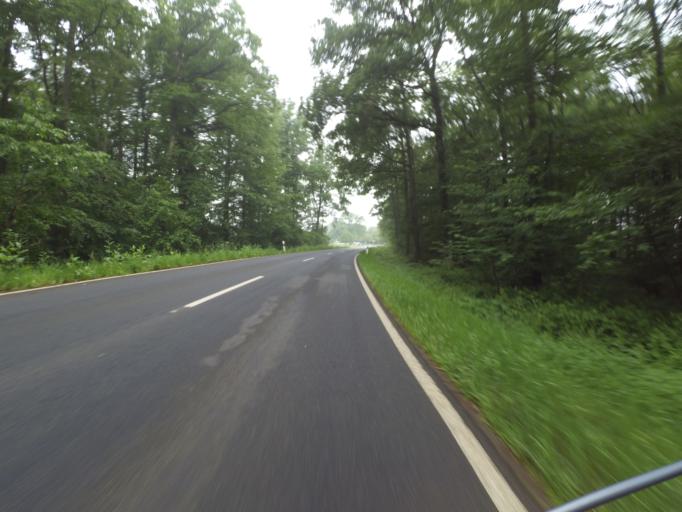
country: DE
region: Rheinland-Pfalz
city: Ernst
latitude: 50.1498
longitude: 7.2267
